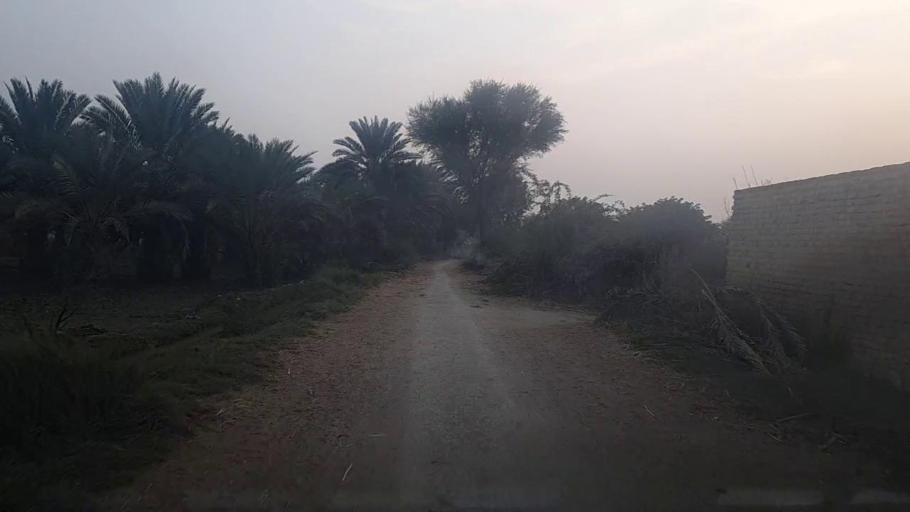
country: PK
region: Sindh
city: Kot Diji
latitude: 27.3397
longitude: 68.6420
